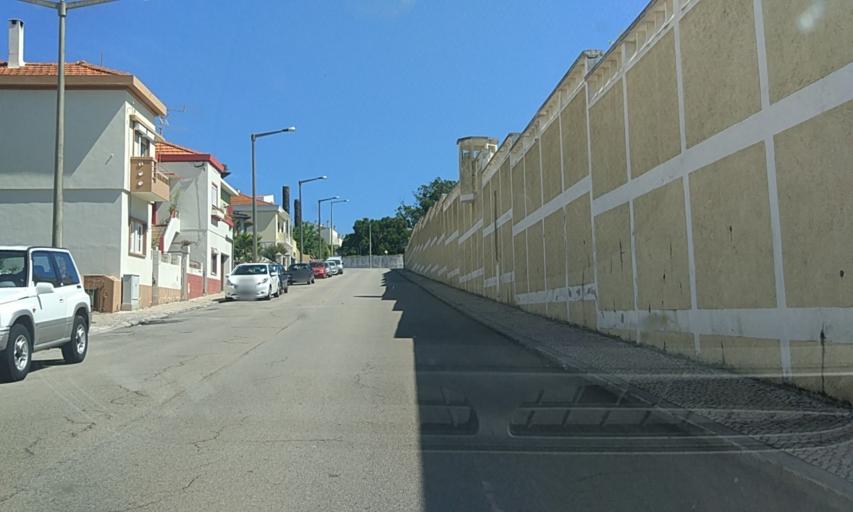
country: PT
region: Coimbra
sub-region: Figueira da Foz
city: Figueira da Foz
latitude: 40.1531
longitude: -8.8528
